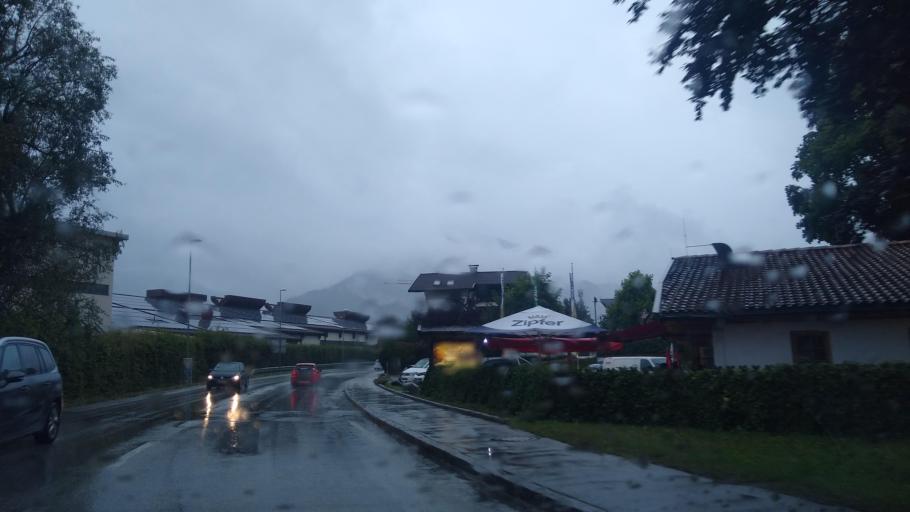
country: AT
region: Tyrol
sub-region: Politischer Bezirk Kufstein
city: Brixlegg
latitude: 47.4294
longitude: 11.8761
